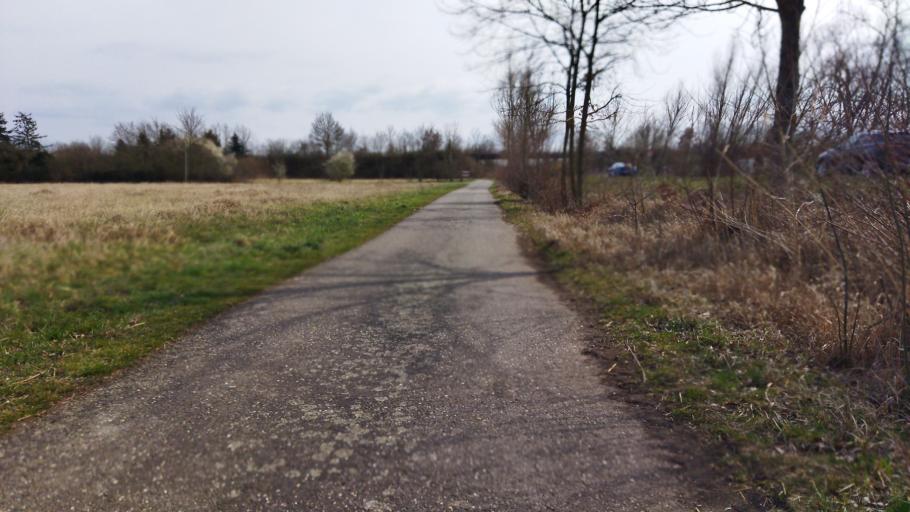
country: DE
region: Rheinland-Pfalz
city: Hassloch
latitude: 49.3606
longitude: 8.2780
